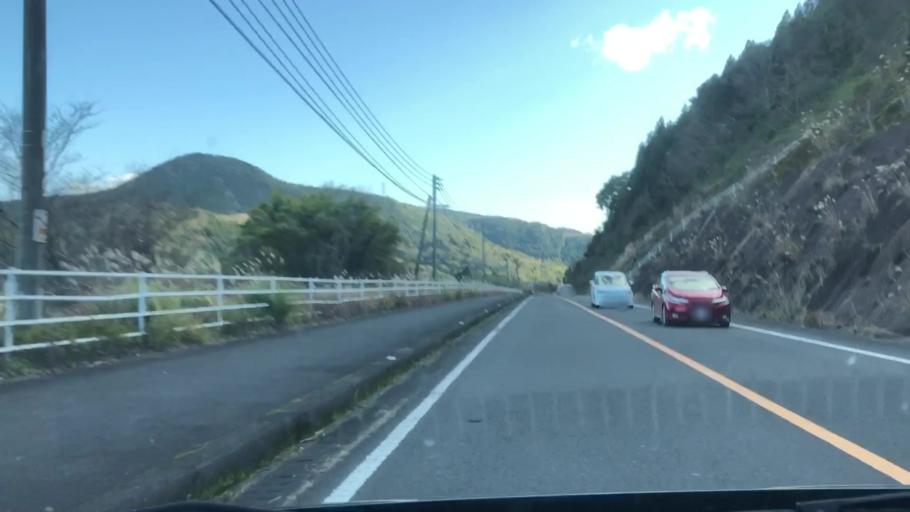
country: JP
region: Kagoshima
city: Satsumasendai
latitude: 31.8560
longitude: 130.3170
